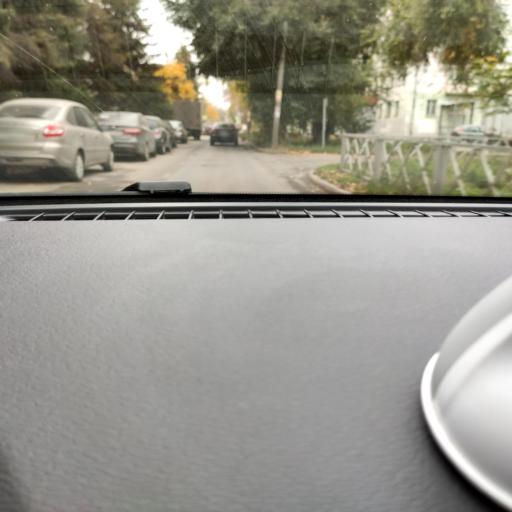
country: RU
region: Samara
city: Samara
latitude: 53.2258
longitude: 50.2677
